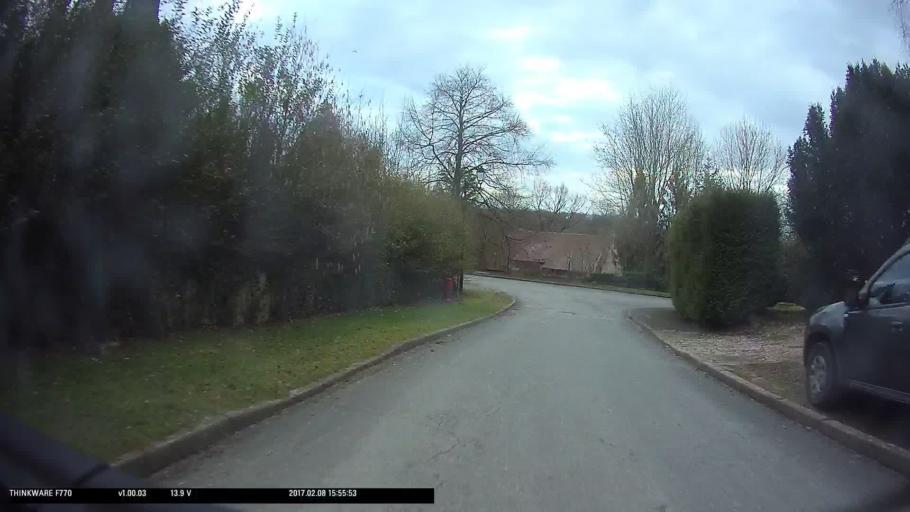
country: FR
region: Ile-de-France
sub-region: Departement du Val-d'Oise
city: Vigny
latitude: 49.0776
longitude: 1.9355
